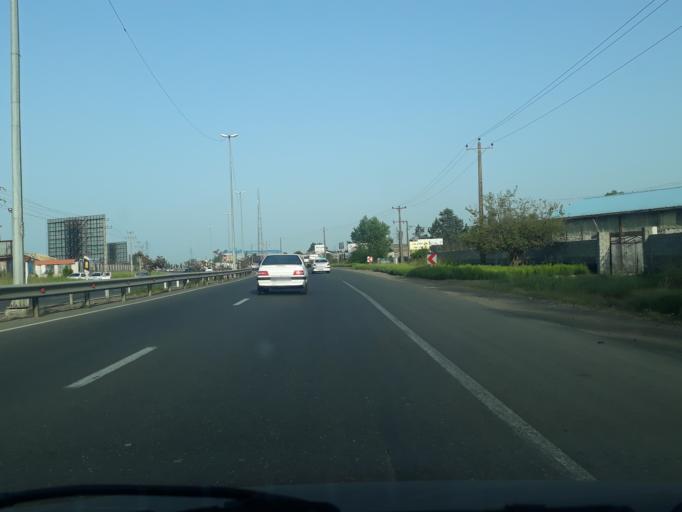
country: IR
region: Gilan
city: Bandar-e Anzali
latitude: 37.4597
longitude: 49.5809
